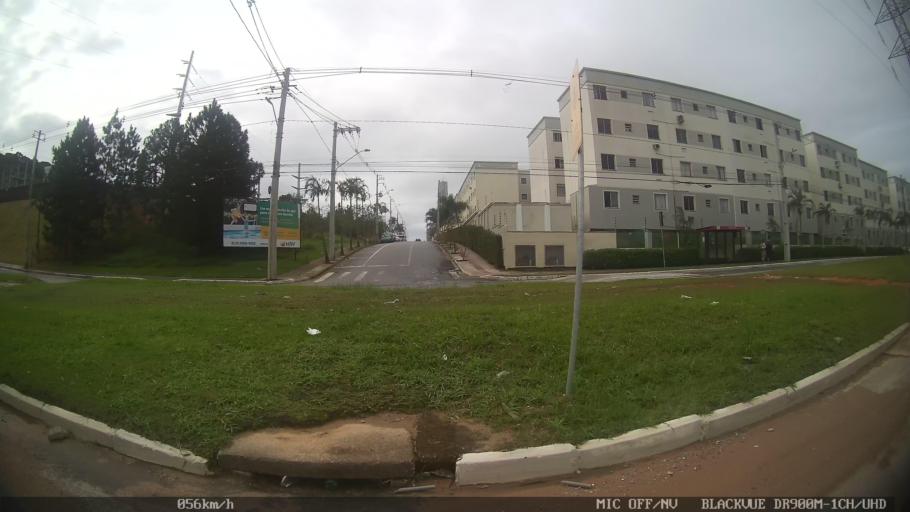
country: BR
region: Santa Catarina
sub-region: Sao Jose
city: Campinas
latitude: -27.5570
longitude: -48.6411
